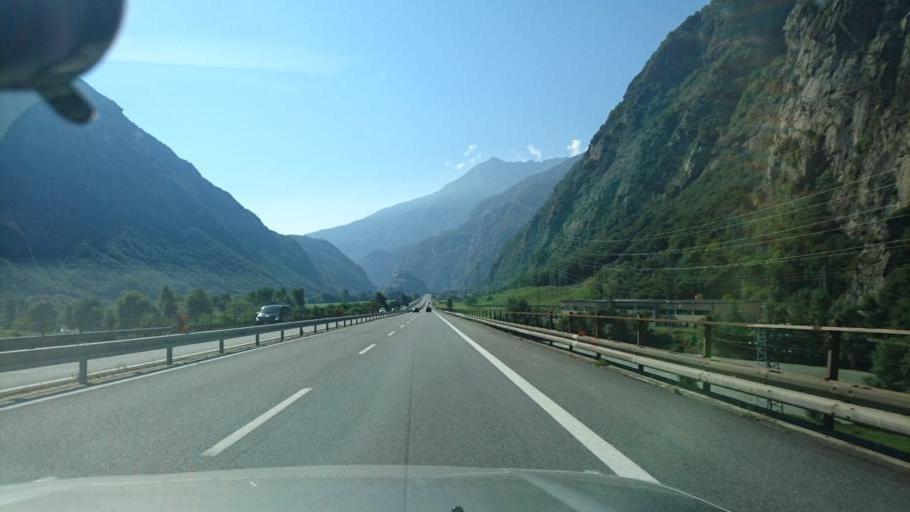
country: IT
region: Aosta Valley
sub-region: Valle d'Aosta
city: Arnad
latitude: 45.6330
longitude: 7.7262
